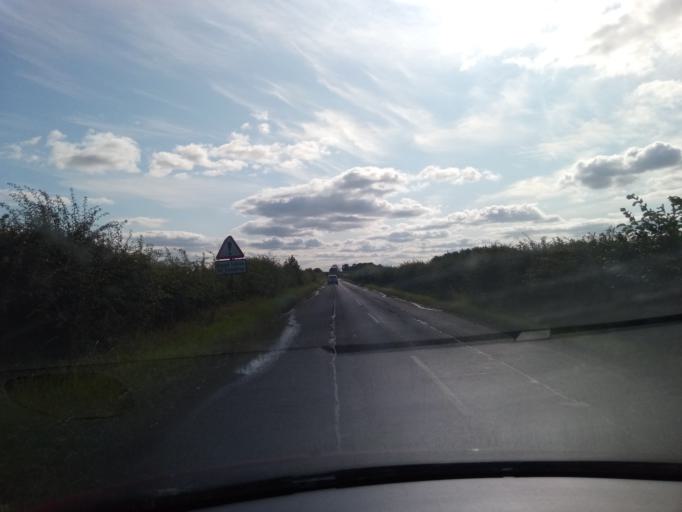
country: GB
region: Scotland
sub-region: The Scottish Borders
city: Allanton
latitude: 55.7474
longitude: -2.1607
